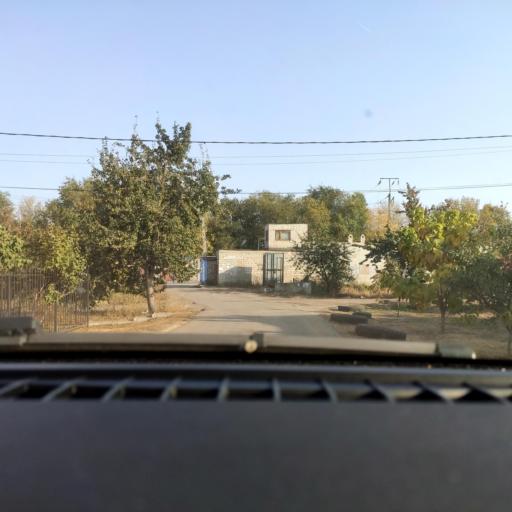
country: RU
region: Voronezj
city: Voronezh
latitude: 51.6732
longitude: 39.2698
